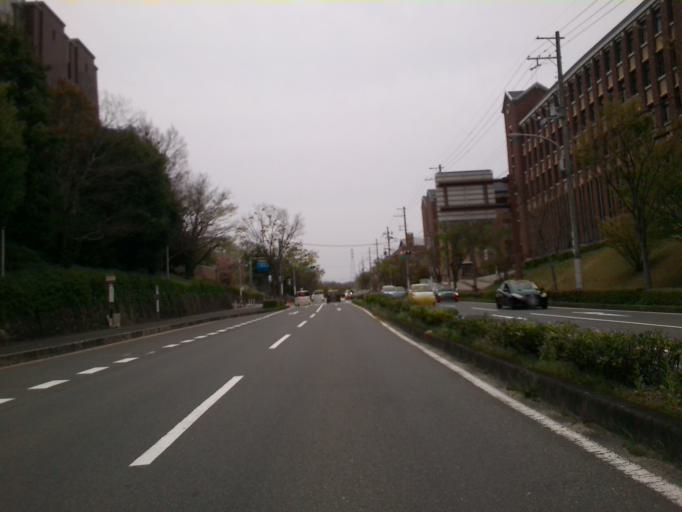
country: JP
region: Kyoto
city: Tanabe
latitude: 34.8030
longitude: 135.7717
